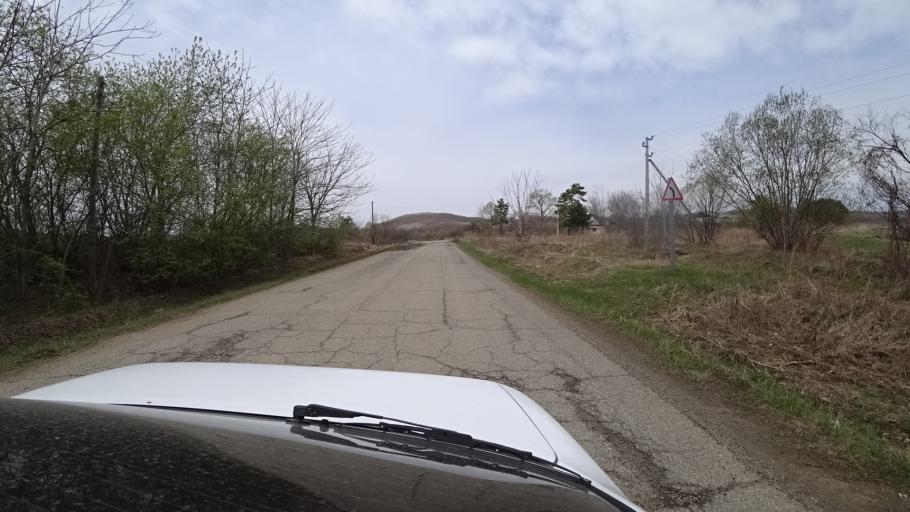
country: RU
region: Primorskiy
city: Dal'nerechensk
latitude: 45.7990
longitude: 134.1013
